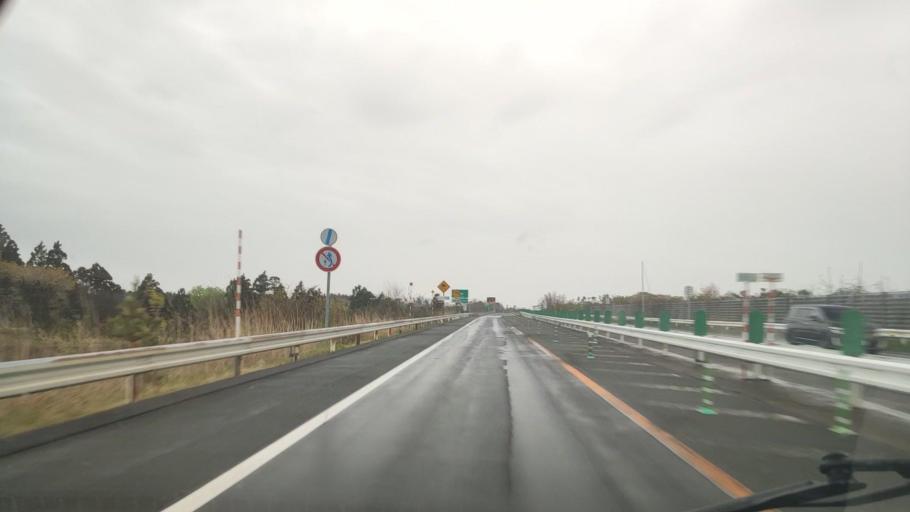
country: JP
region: Akita
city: Noshiromachi
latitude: 40.1272
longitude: 140.0125
